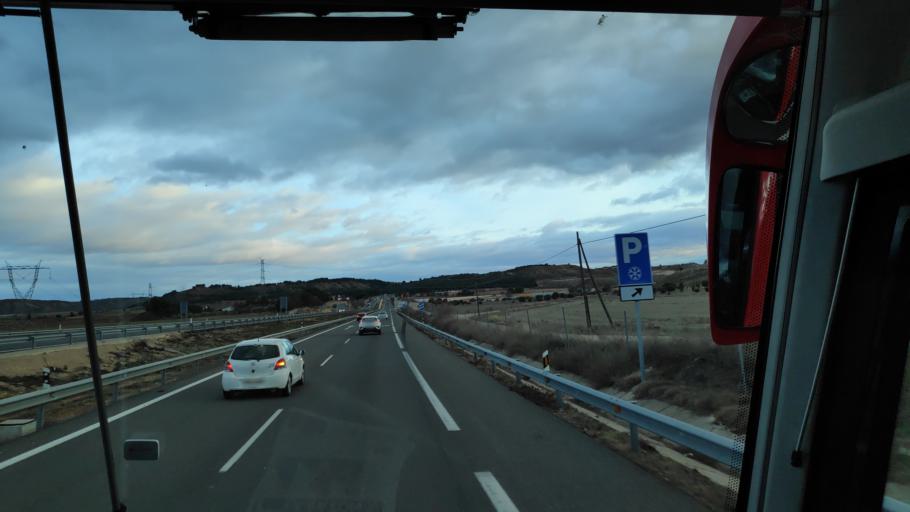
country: ES
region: Castille-La Mancha
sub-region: Provincia de Cuenca
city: Belinchon
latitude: 40.0409
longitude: -3.0528
